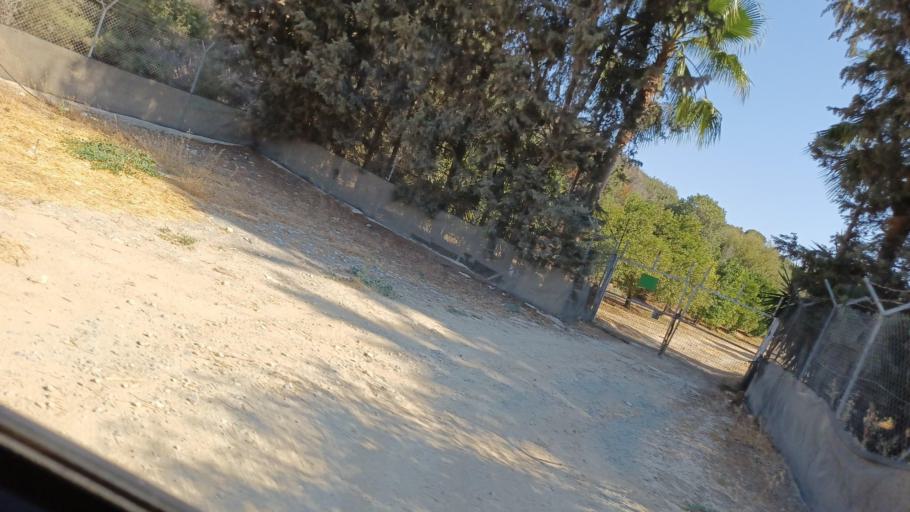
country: CY
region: Limassol
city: Pissouri
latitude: 34.7113
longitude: 32.6809
